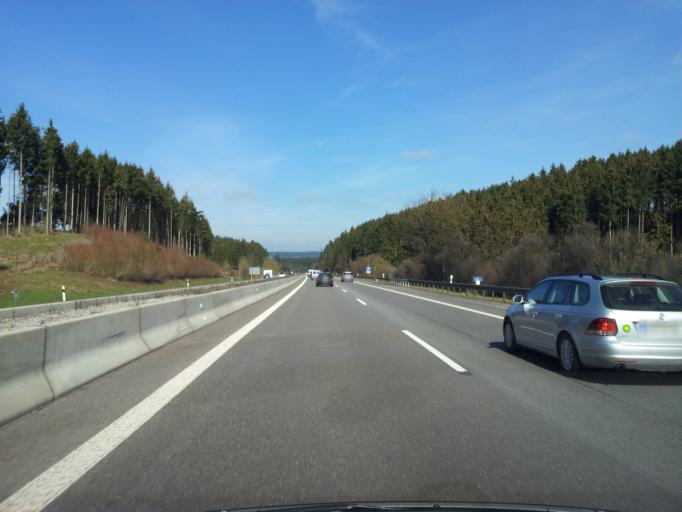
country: DE
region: Baden-Wuerttemberg
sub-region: Freiburg Region
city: Trossingen
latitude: 48.0640
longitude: 8.6145
